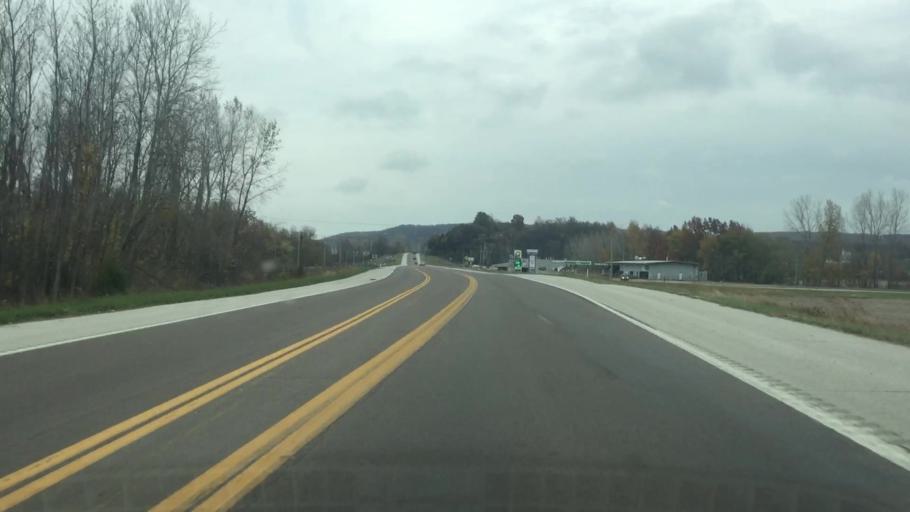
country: US
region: Missouri
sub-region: Gasconade County
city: Hermann
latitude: 38.7272
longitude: -91.4456
